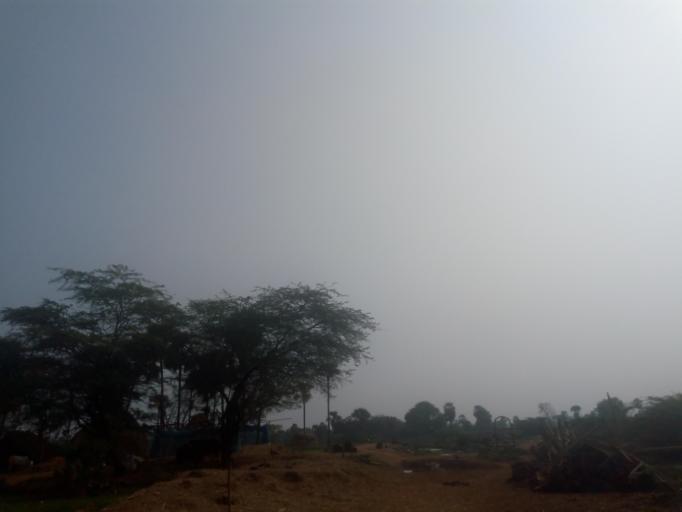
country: IN
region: Andhra Pradesh
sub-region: West Godavari
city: Tadepallegudem
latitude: 16.8608
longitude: 81.3154
